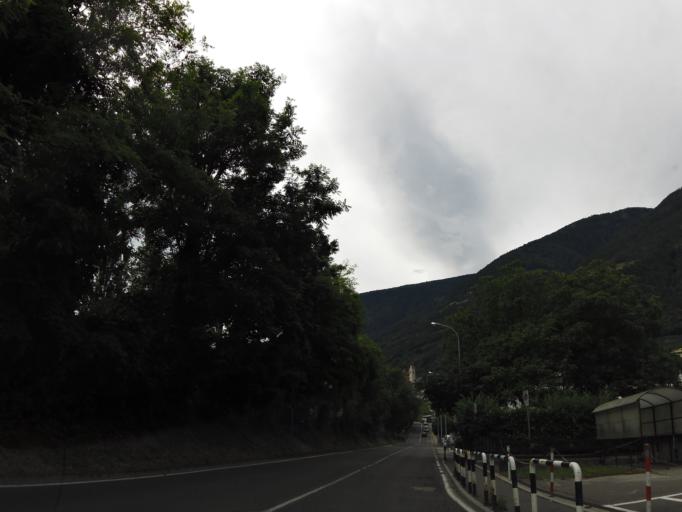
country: IT
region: Trentino-Alto Adige
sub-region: Bolzano
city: Marlengo
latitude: 46.6609
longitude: 11.1484
